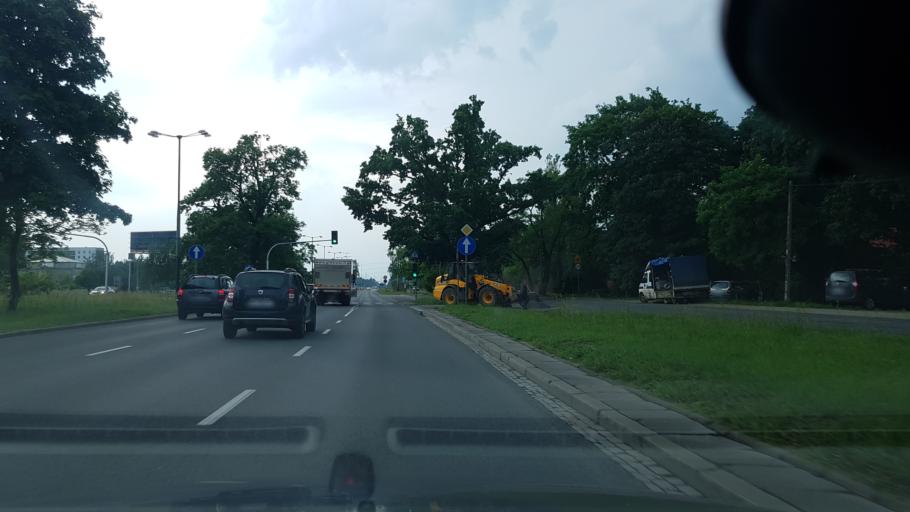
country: PL
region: Masovian Voivodeship
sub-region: Warszawa
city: Bialoleka
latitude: 52.3467
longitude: 20.9493
